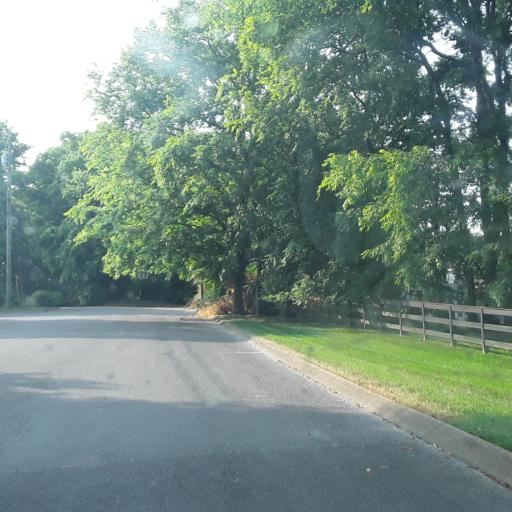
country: US
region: Tennessee
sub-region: Williamson County
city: Brentwood
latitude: 36.0589
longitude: -86.7502
